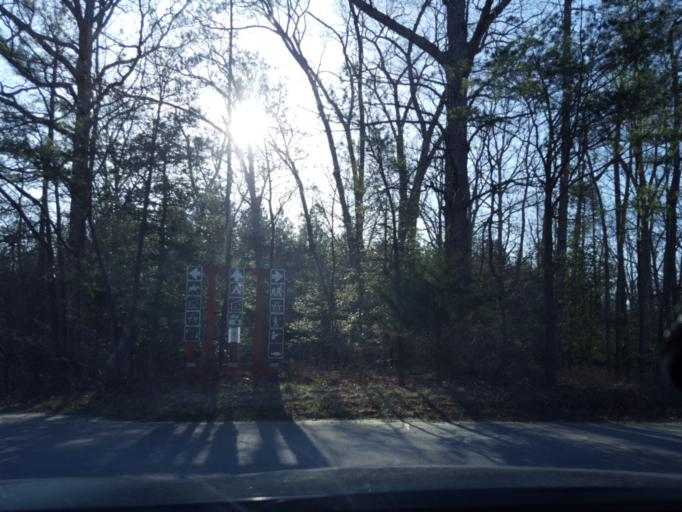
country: US
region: Maryland
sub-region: Prince George's County
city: Baden
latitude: 38.6469
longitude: -76.8181
